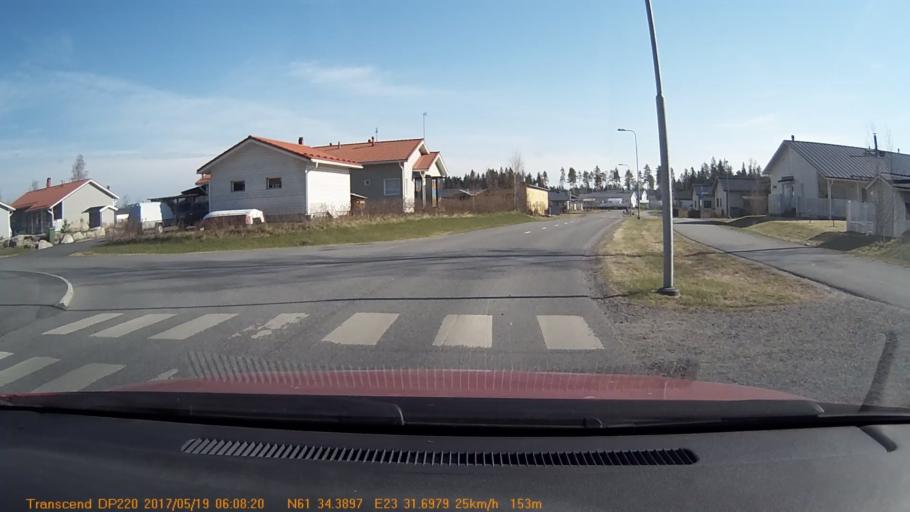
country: FI
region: Pirkanmaa
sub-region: Tampere
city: Yloejaervi
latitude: 61.5732
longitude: 23.5283
